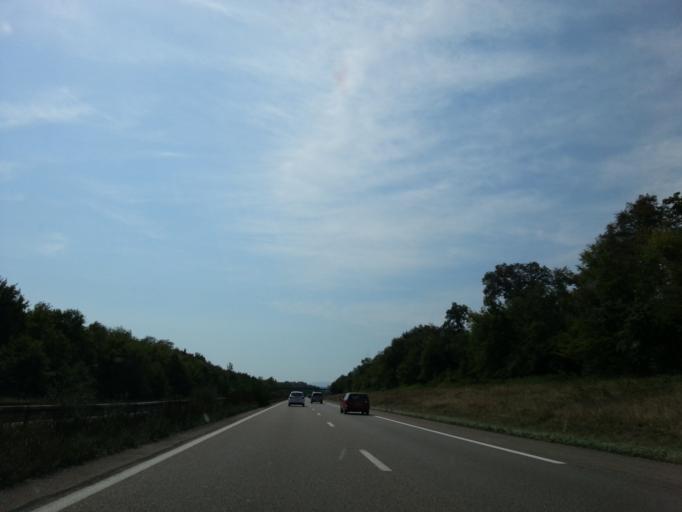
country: FR
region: Alsace
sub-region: Departement du Haut-Rhin
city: Bartenheim
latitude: 47.6553
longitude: 7.4881
